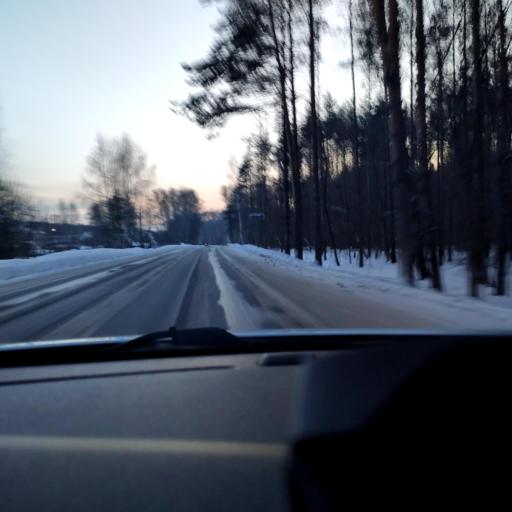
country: RU
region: Tatarstan
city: Vysokaya Gora
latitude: 55.9032
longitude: 49.2667
